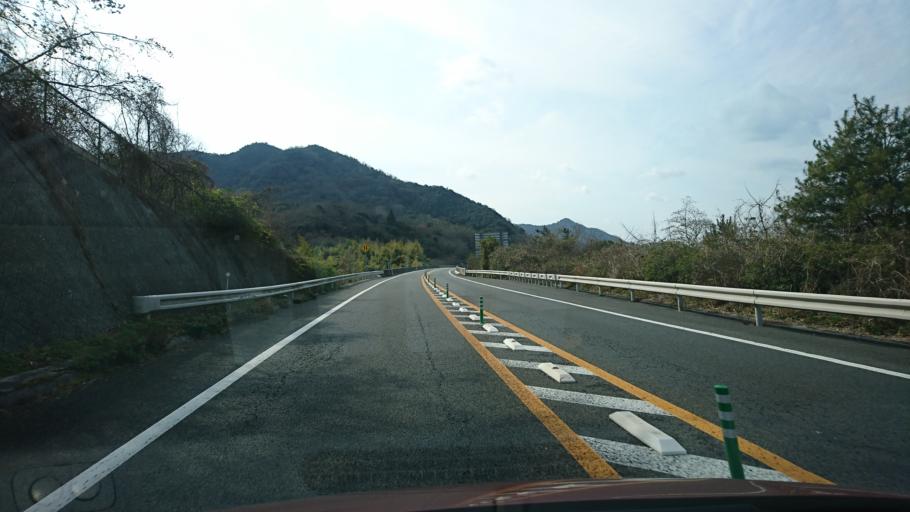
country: JP
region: Hiroshima
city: Innoshima
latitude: 34.1362
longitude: 133.0526
